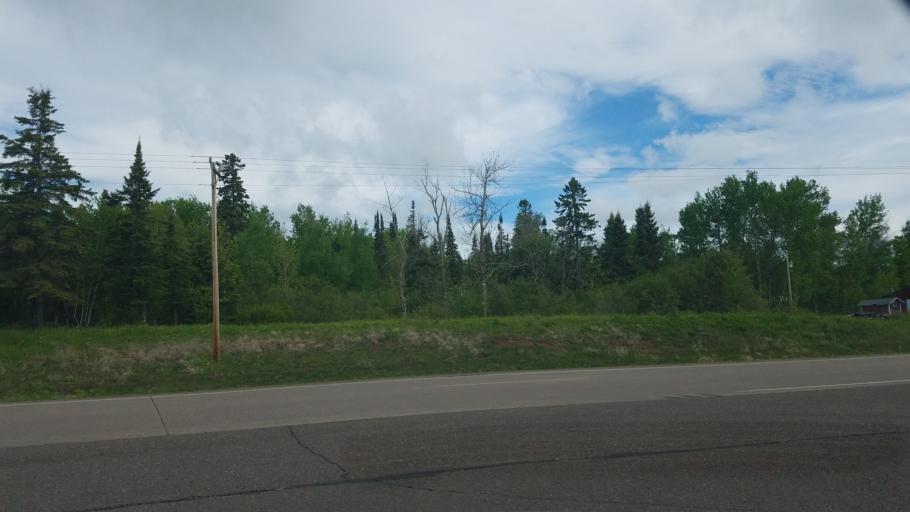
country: US
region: Minnesota
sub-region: Lake County
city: Two Harbors
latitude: 47.1204
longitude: -91.5043
